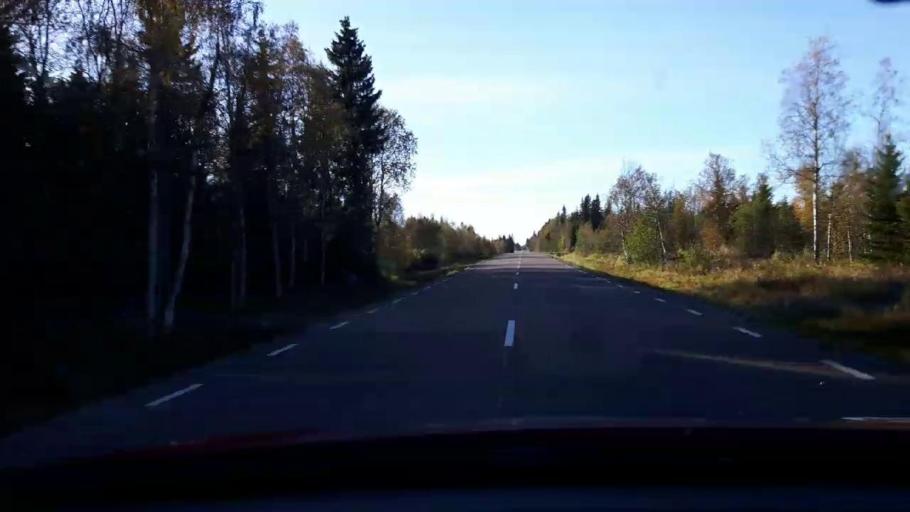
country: SE
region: Jaemtland
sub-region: Stroemsunds Kommun
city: Stroemsund
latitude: 63.8607
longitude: 15.1790
